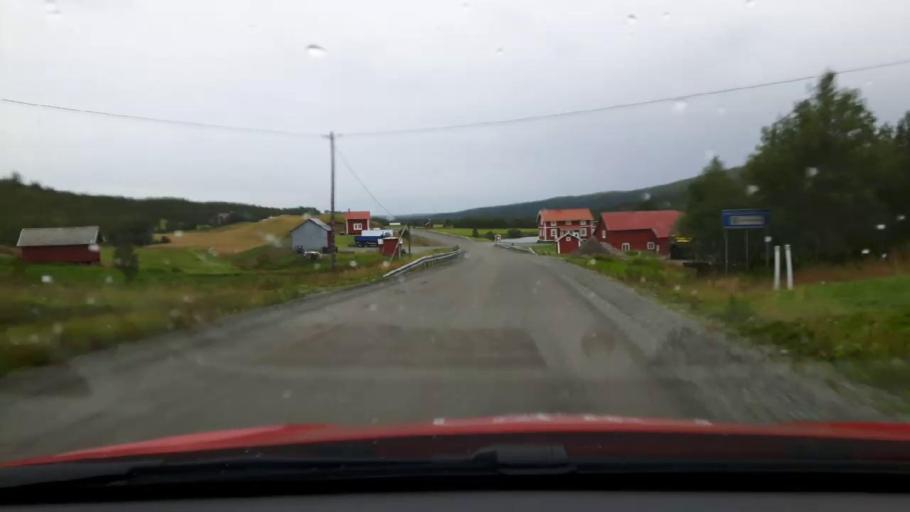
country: NO
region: Nord-Trondelag
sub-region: Meraker
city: Meraker
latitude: 63.5302
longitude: 12.3924
